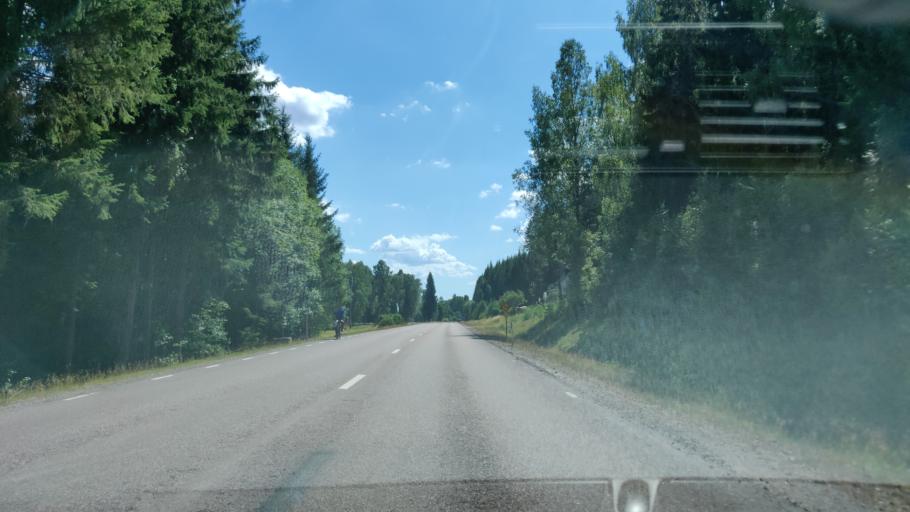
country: SE
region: Vaermland
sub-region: Hagfors Kommun
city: Ekshaerad
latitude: 60.1916
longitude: 13.4976
